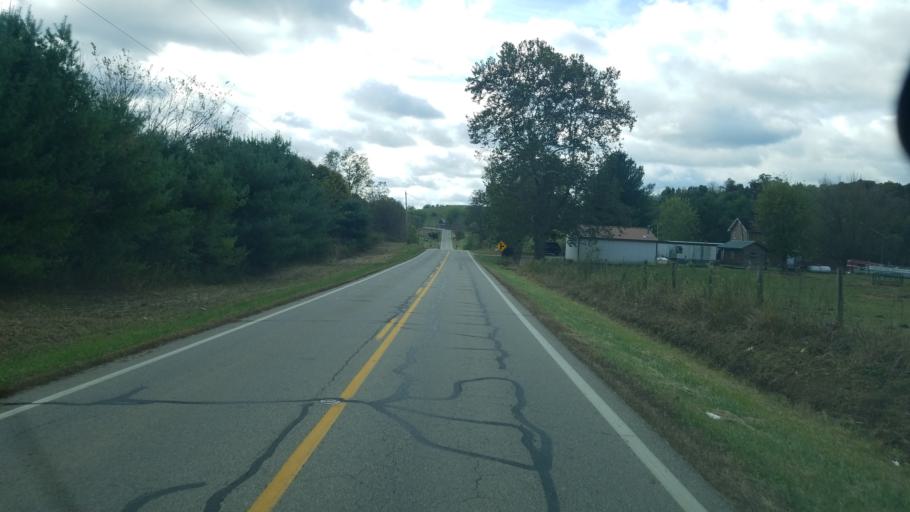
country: US
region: Ohio
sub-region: Jackson County
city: Wellston
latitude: 39.1754
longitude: -82.5255
